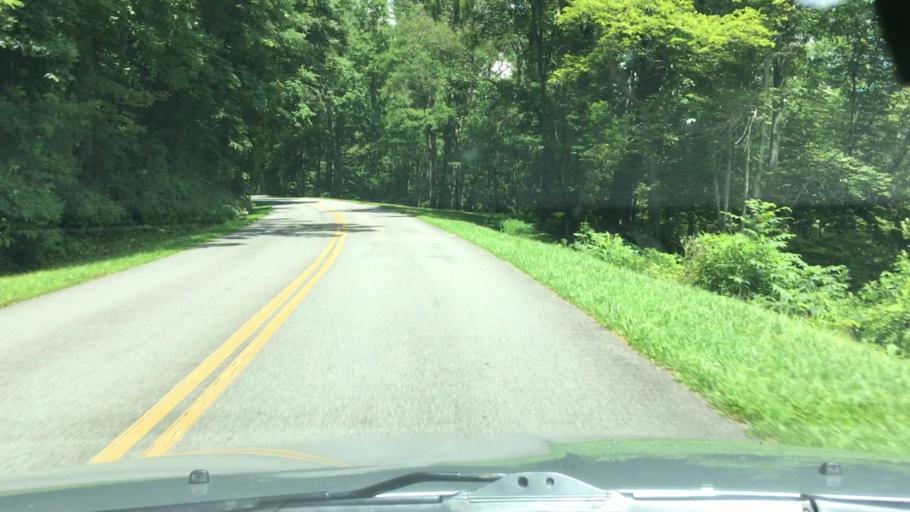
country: US
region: North Carolina
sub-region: Buncombe County
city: Asheville
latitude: 35.6364
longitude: -82.4909
